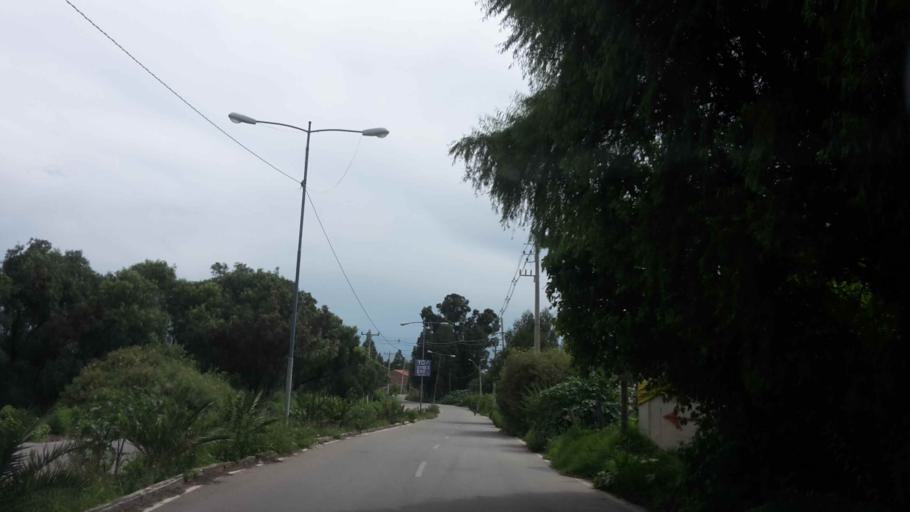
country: BO
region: Cochabamba
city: Cochabamba
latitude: -17.3304
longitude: -66.2487
